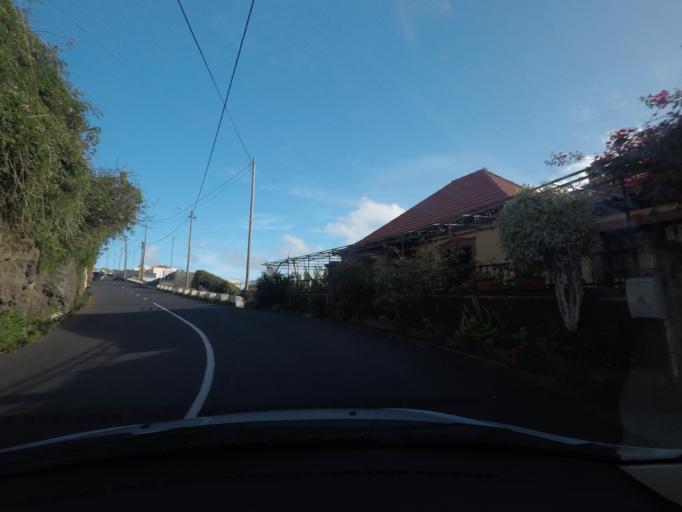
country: PT
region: Madeira
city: Ribeira Brava
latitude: 32.6709
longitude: -17.0605
